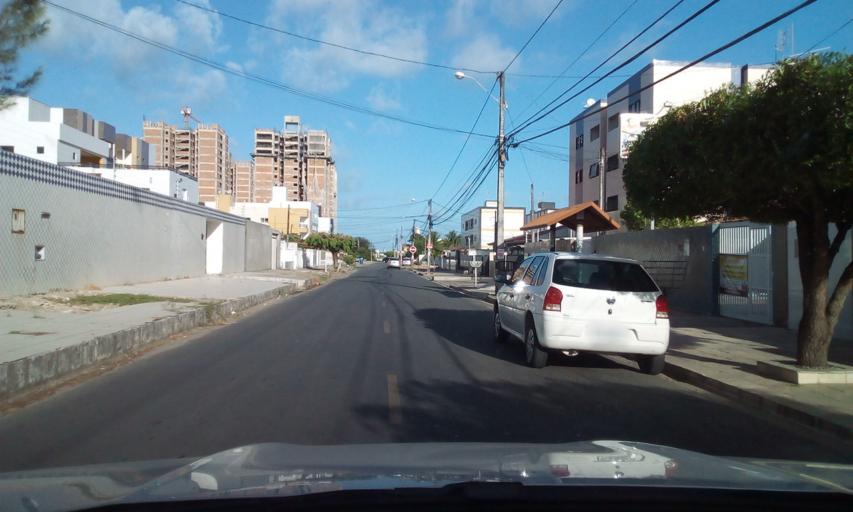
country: BR
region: Paraiba
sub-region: Joao Pessoa
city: Joao Pessoa
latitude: -7.1558
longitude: -34.8276
